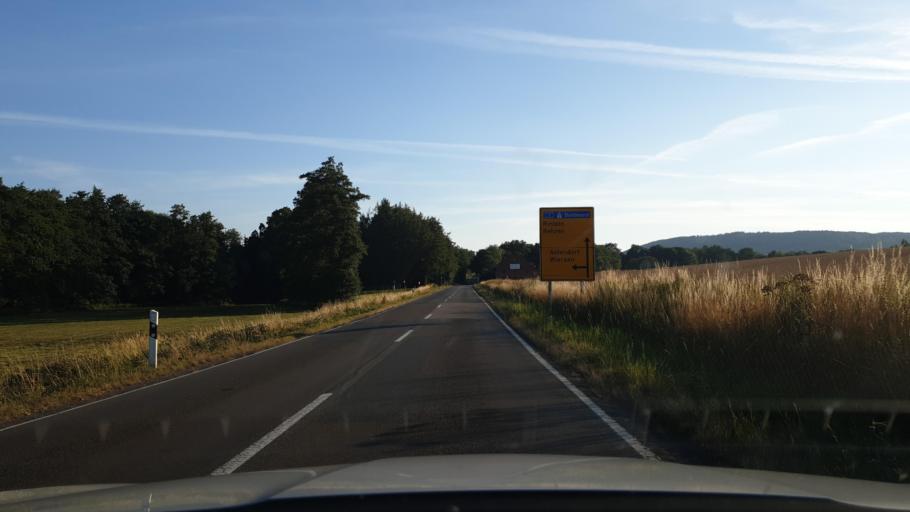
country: DE
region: Lower Saxony
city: Apelern
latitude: 52.2847
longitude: 9.3110
